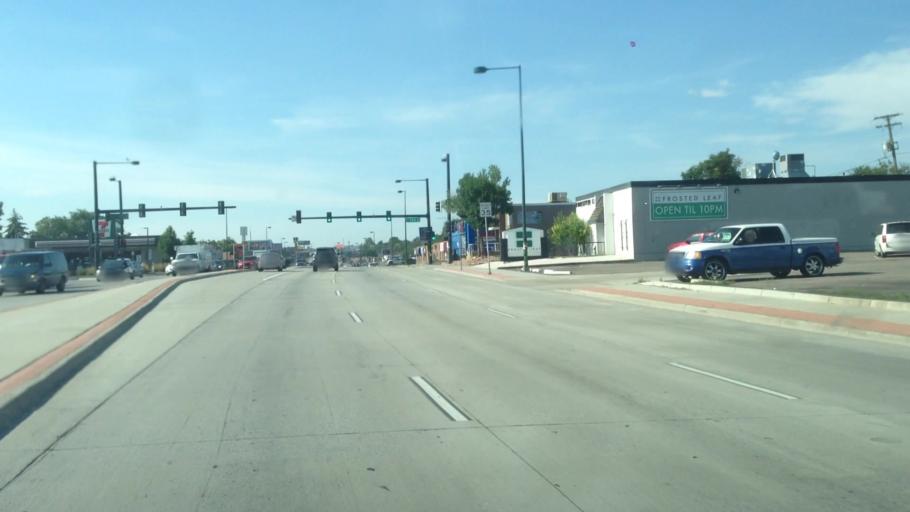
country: US
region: Colorado
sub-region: Denver County
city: Denver
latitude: 39.7243
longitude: -105.0251
